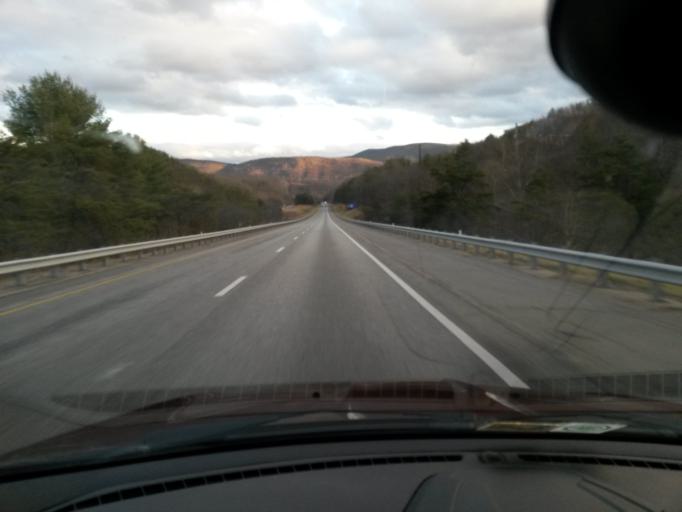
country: US
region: Virginia
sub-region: City of Covington
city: Covington
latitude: 37.7821
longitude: -80.0094
